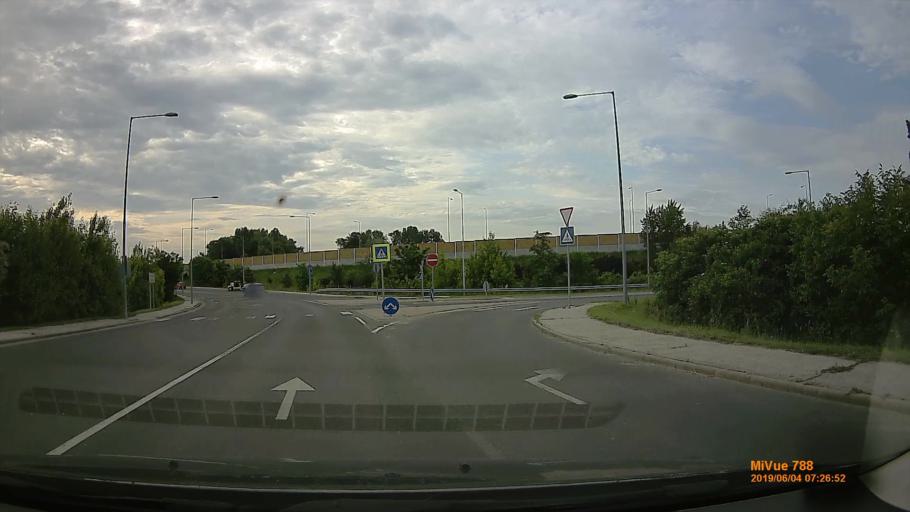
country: HU
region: Pest
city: Diosd
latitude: 47.4024
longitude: 18.9769
